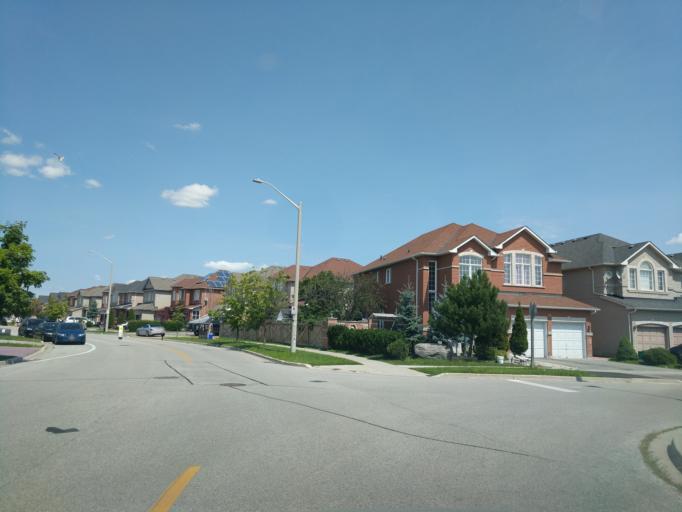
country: CA
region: Ontario
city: Markham
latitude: 43.8451
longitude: -79.2453
